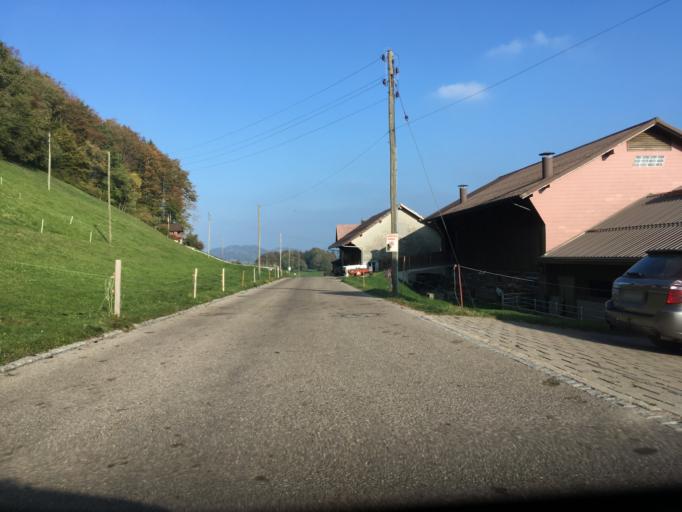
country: CH
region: Saint Gallen
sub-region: Wahlkreis Toggenburg
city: Mosnang
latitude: 47.3393
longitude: 9.0402
